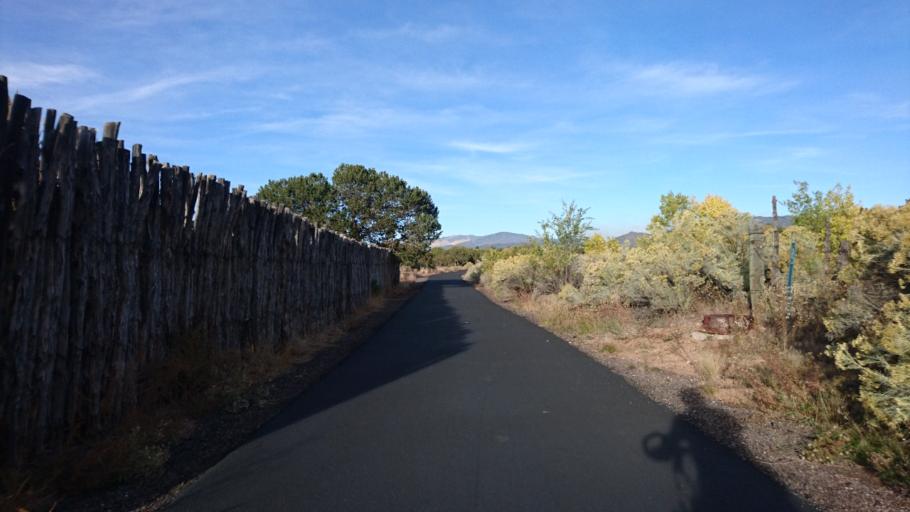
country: US
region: New Mexico
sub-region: Santa Fe County
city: Agua Fria
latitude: 35.6461
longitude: -105.9724
